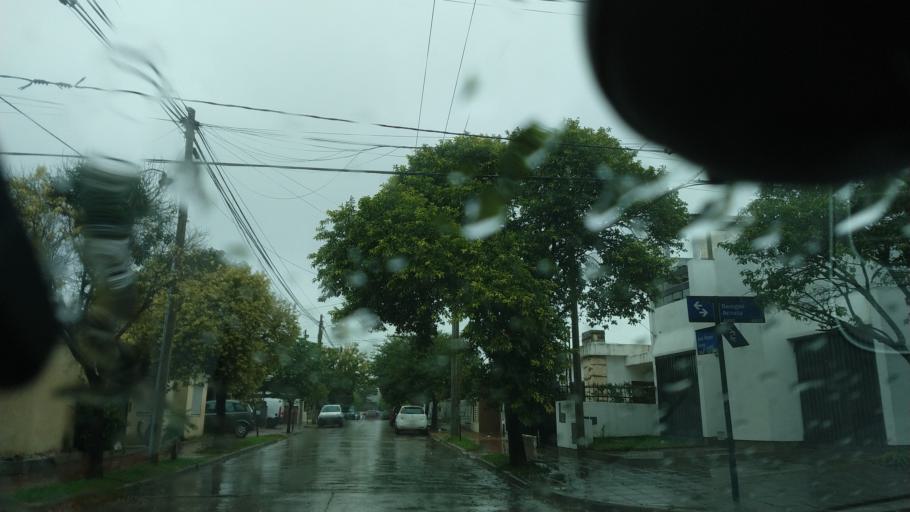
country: AR
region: Cordoba
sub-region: Departamento de Capital
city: Cordoba
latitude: -31.3668
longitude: -64.2316
